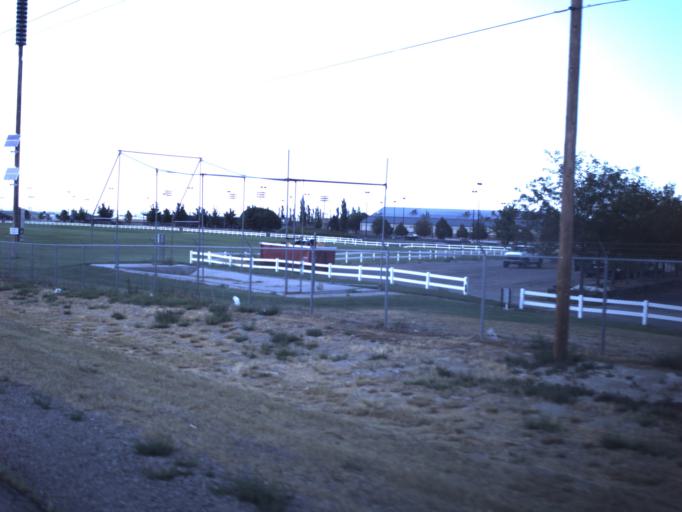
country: US
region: Utah
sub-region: Tooele County
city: Erda
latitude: 40.5683
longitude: -112.3705
